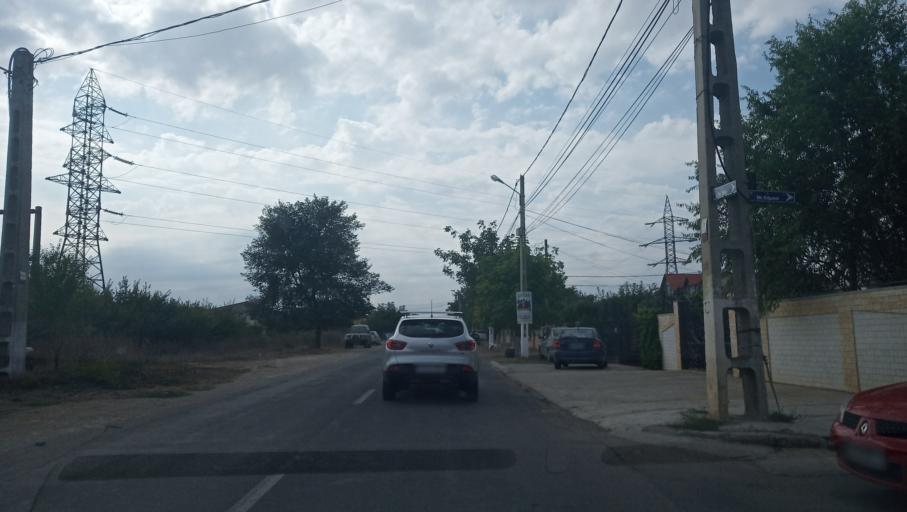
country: RO
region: Constanta
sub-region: Municipiul Mangalia
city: Mangalia
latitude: 43.8153
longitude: 28.5646
